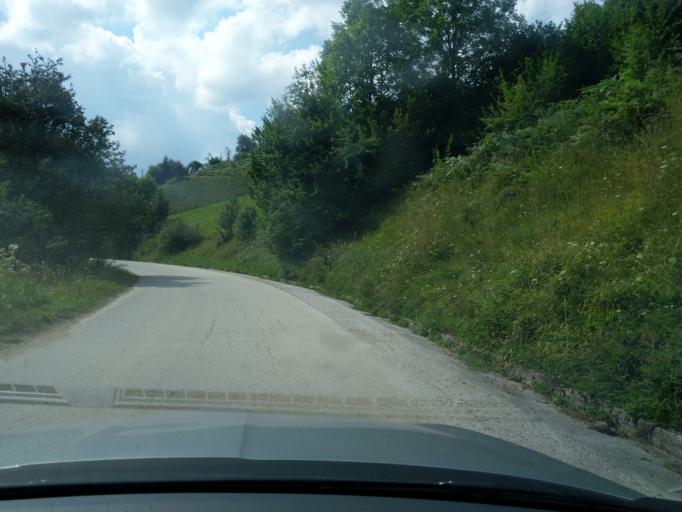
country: RS
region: Central Serbia
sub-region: Zlatiborski Okrug
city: Nova Varos
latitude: 43.5905
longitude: 19.8608
